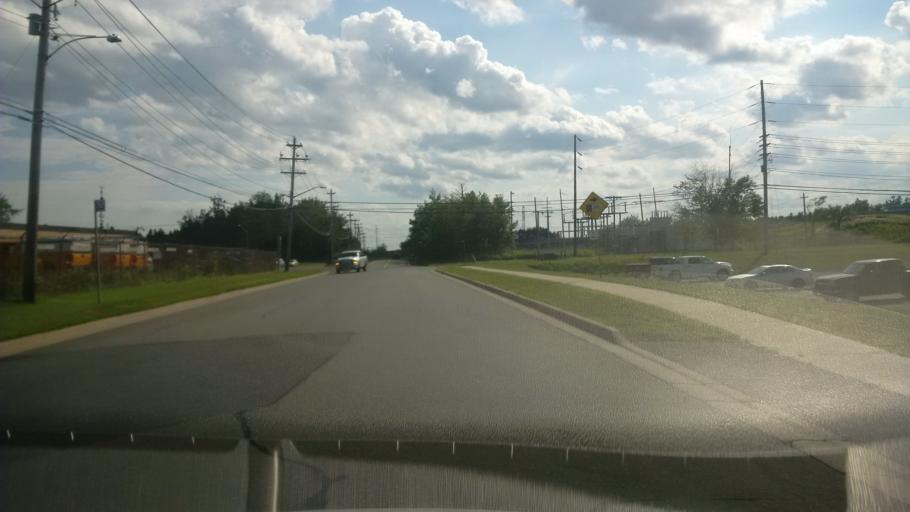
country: CA
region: New Brunswick
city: Fredericton
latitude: 45.9386
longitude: -66.6486
